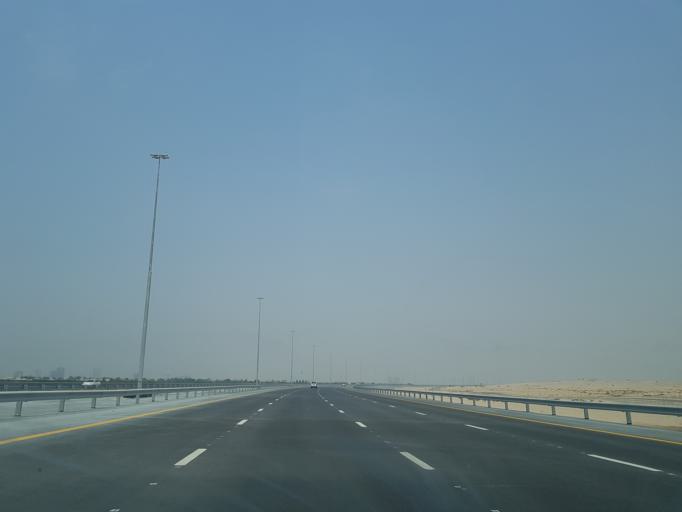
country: AE
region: Dubai
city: Dubai
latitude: 25.0075
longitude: 55.1960
